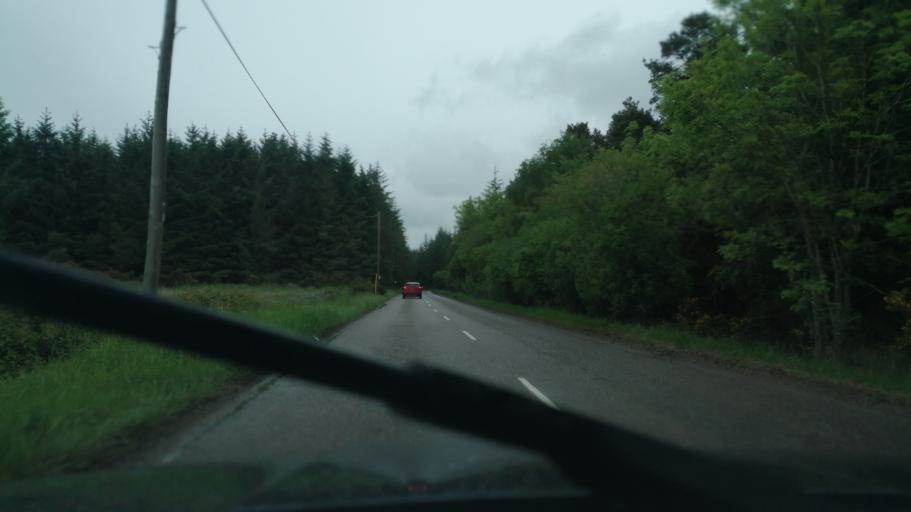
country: GB
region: Scotland
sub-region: Aberdeenshire
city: Portsoy
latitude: 57.6296
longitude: -2.7185
